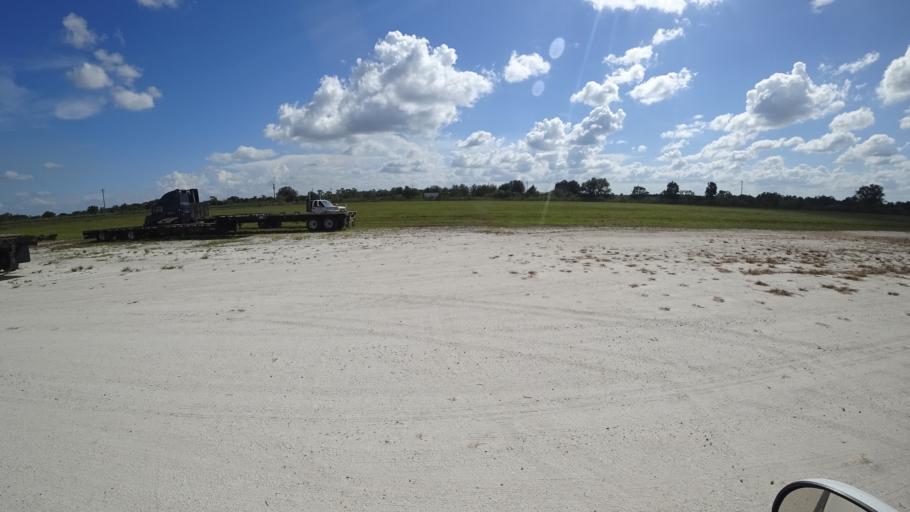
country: US
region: Florida
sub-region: DeSoto County
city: Arcadia
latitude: 27.3127
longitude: -82.1020
